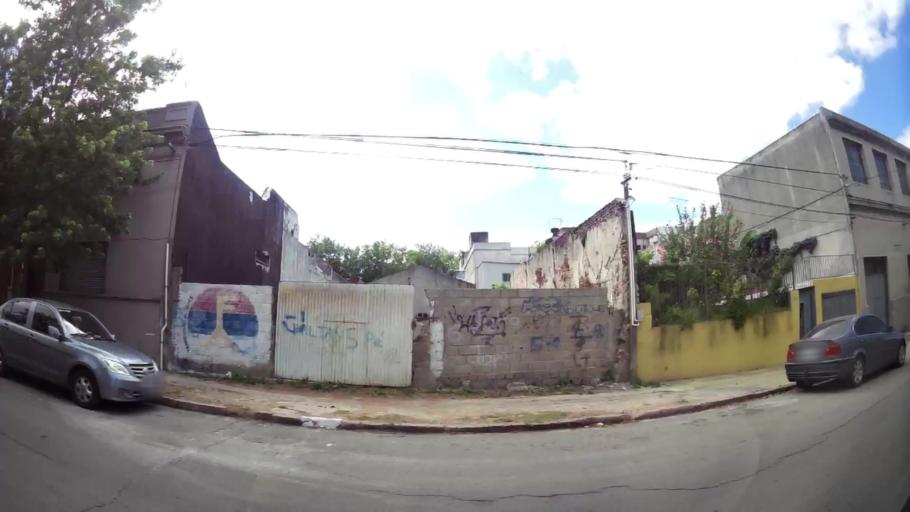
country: UY
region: Montevideo
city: Montevideo
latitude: -34.8784
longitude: -56.1816
